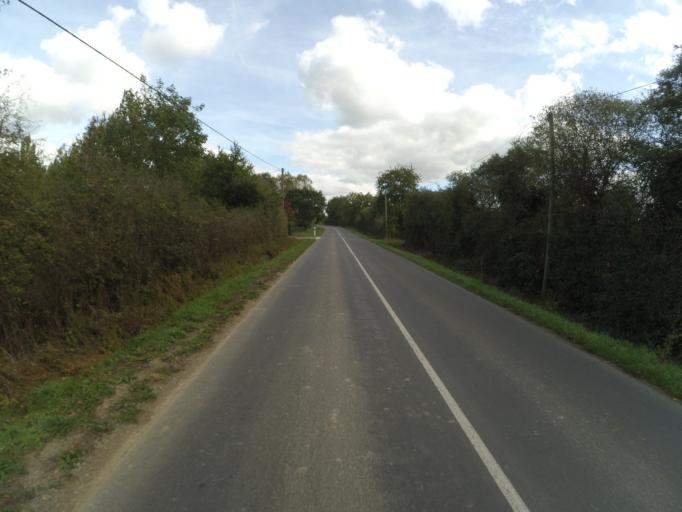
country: FR
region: Pays de la Loire
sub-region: Departement de la Loire-Atlantique
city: Heric
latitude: 47.4098
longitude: -1.6278
